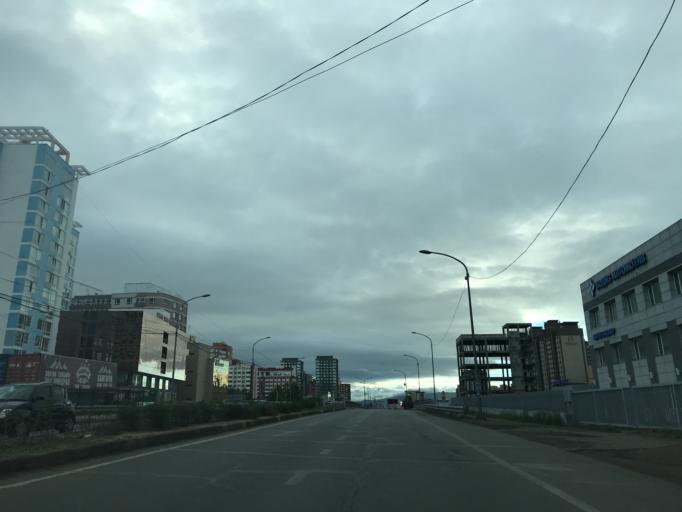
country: MN
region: Ulaanbaatar
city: Ulaanbaatar
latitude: 47.9081
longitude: 106.9311
